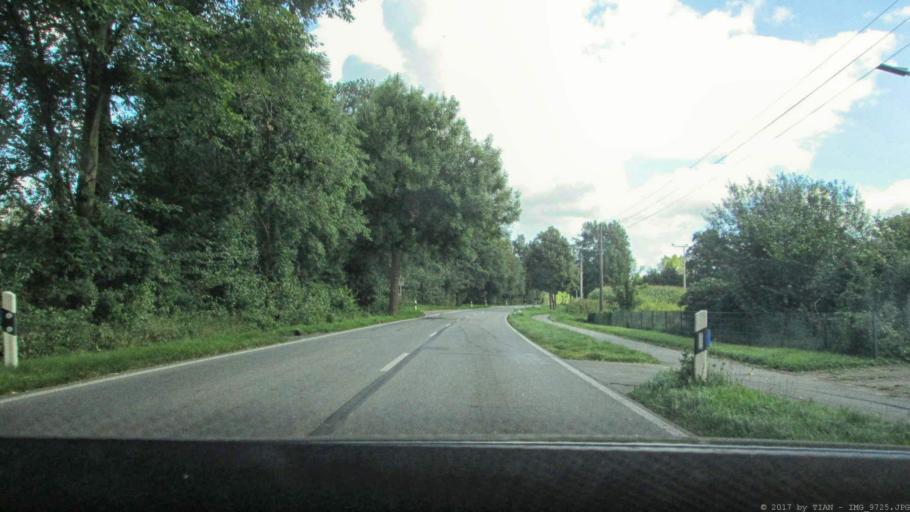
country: DE
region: Schleswig-Holstein
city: Kayhude
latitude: 53.7564
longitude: 10.1449
